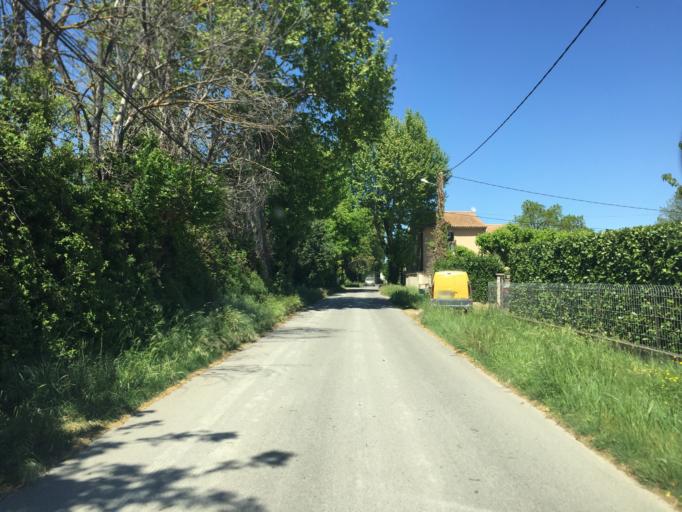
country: FR
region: Provence-Alpes-Cote d'Azur
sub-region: Departement du Vaucluse
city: Jonquieres
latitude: 44.1233
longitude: 4.9066
